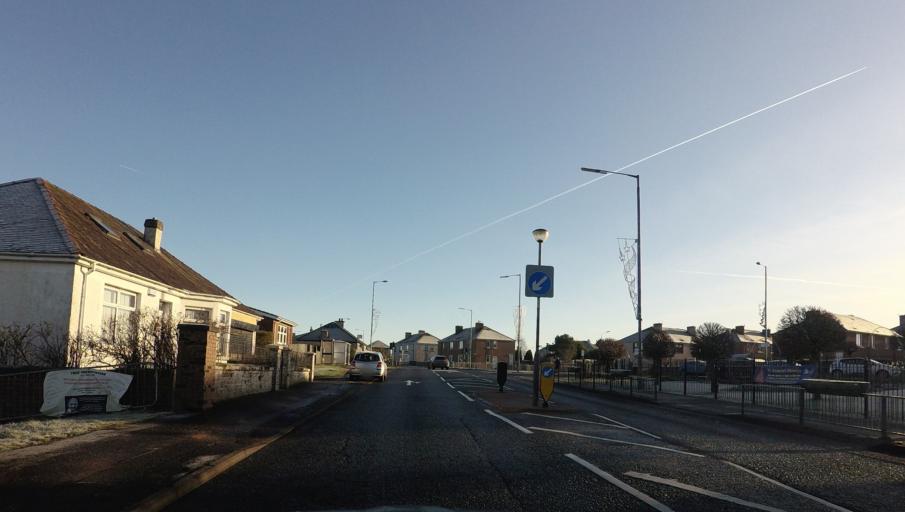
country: GB
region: Scotland
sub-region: North Lanarkshire
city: Shotts
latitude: 55.8003
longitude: -3.8348
